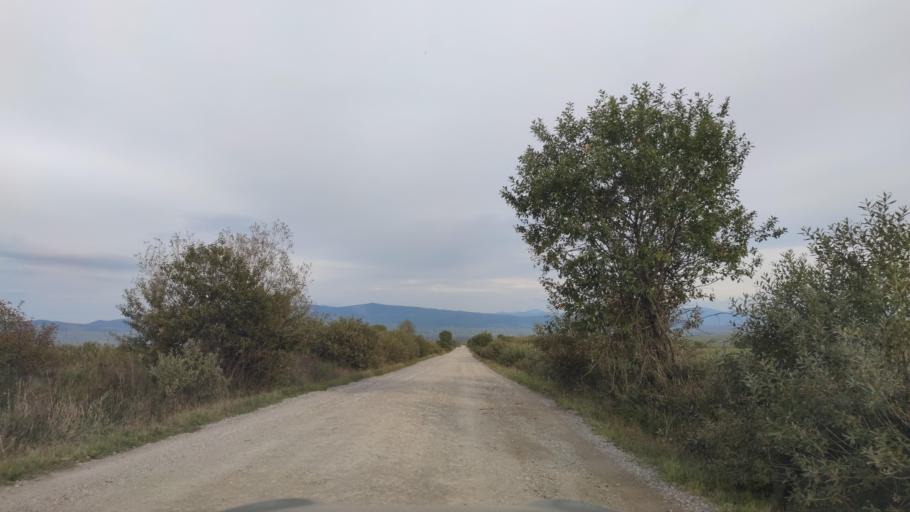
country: RO
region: Harghita
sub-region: Comuna Remetea
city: Remetea
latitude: 46.8108
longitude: 25.3915
